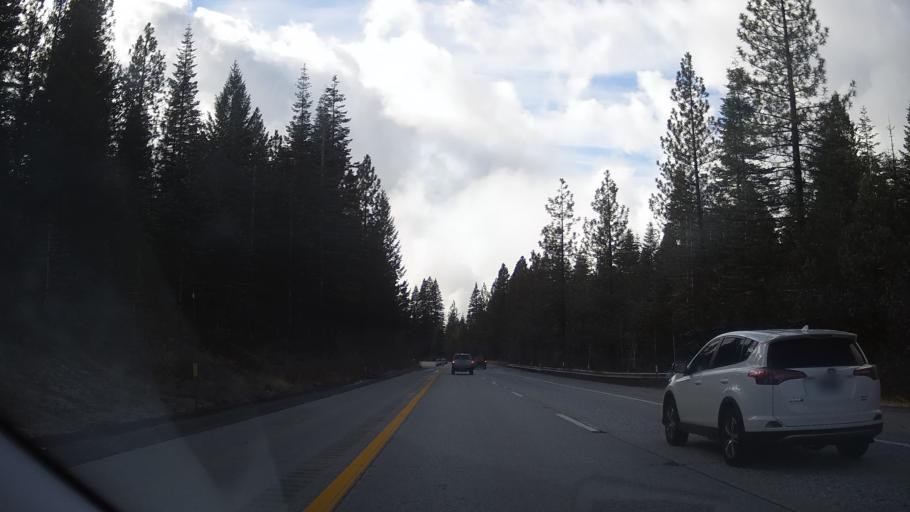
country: US
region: California
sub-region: Placer County
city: Foresthill
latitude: 39.2688
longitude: -120.7224
